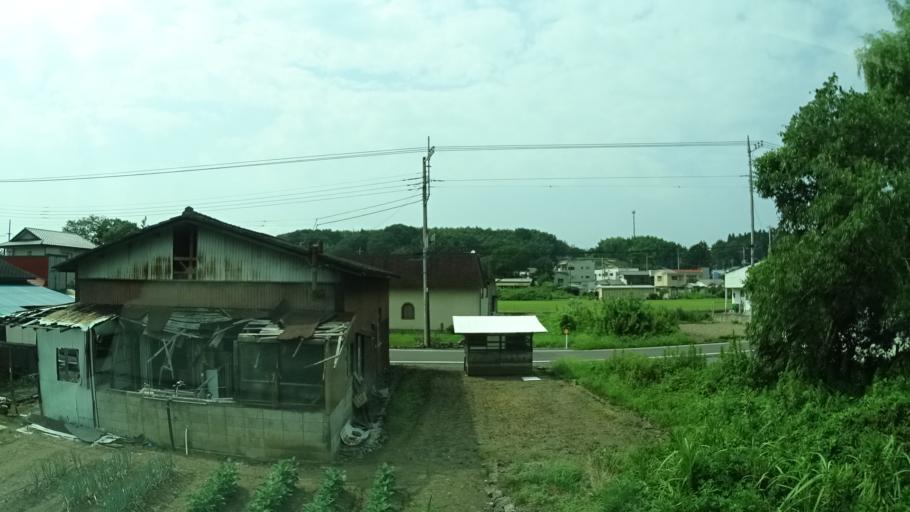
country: JP
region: Tochigi
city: Mashiko
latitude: 36.5374
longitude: 140.1097
